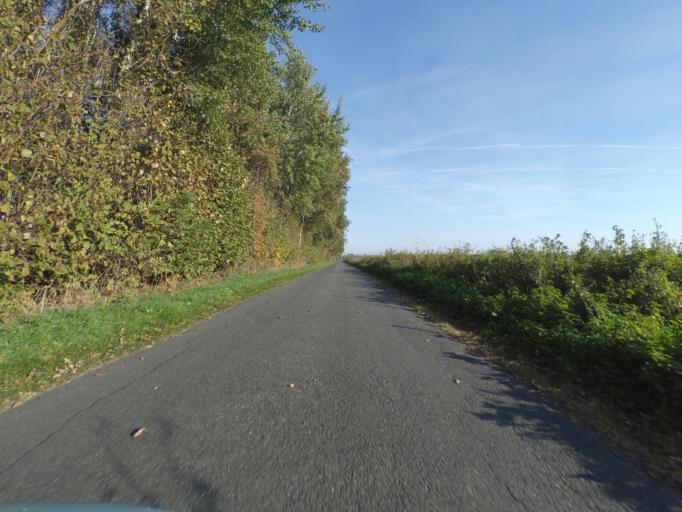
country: NL
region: Gelderland
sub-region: Berkelland
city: Eibergen
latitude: 52.0645
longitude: 6.7240
